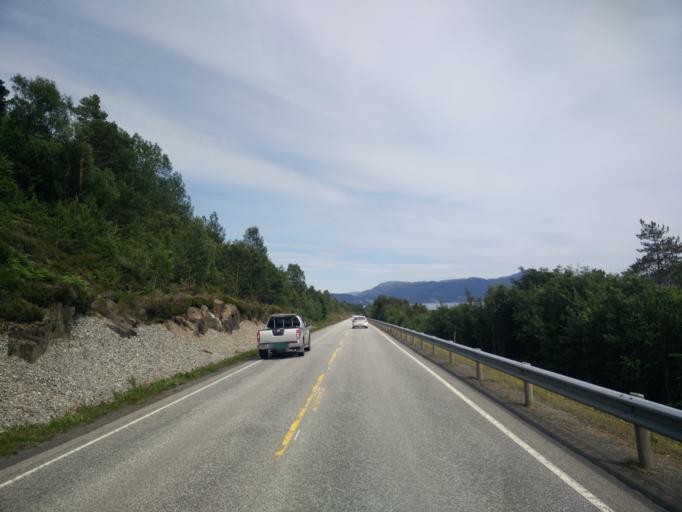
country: NO
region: More og Romsdal
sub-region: Kristiansund
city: Rensvik
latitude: 62.9731
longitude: 7.8346
